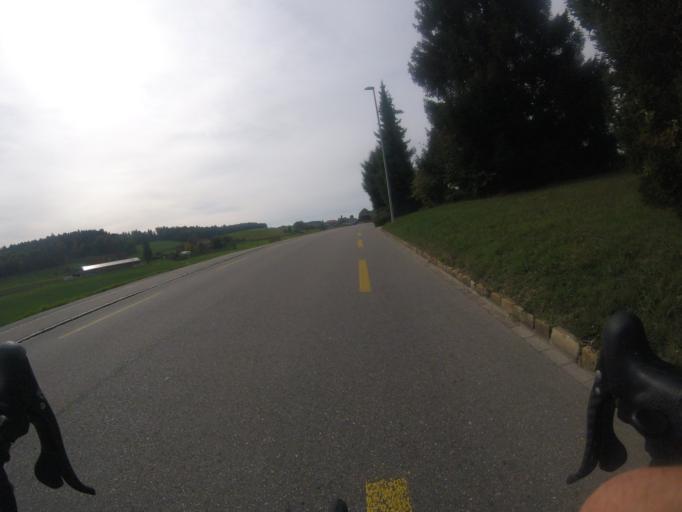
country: CH
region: Bern
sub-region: Bern-Mittelland District
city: Frauenkappelen
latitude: 46.9363
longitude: 7.3607
